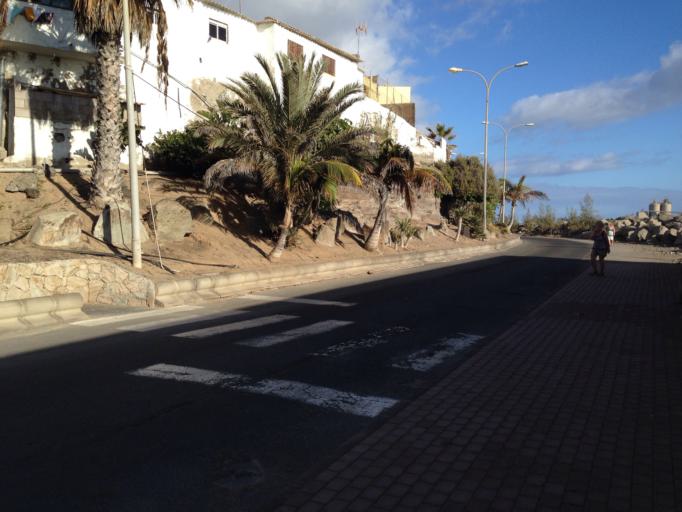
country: ES
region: Canary Islands
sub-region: Provincia de Las Palmas
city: Puerto Rico
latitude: 27.7559
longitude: -15.6840
